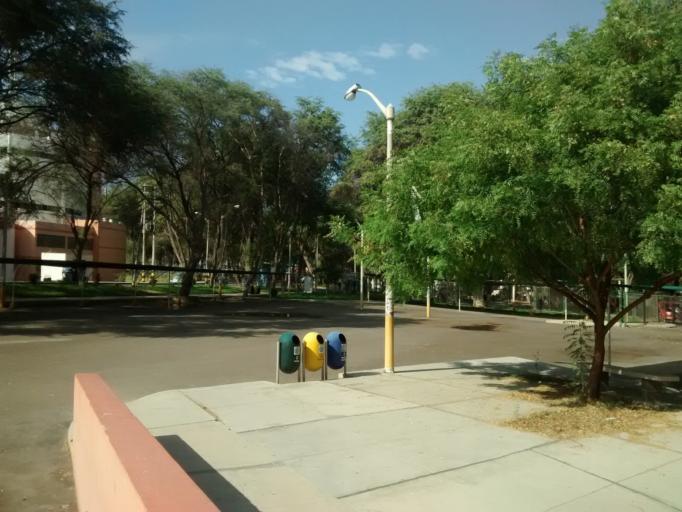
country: PE
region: Piura
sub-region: Provincia de Piura
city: Piura
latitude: -5.1795
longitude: -80.6195
